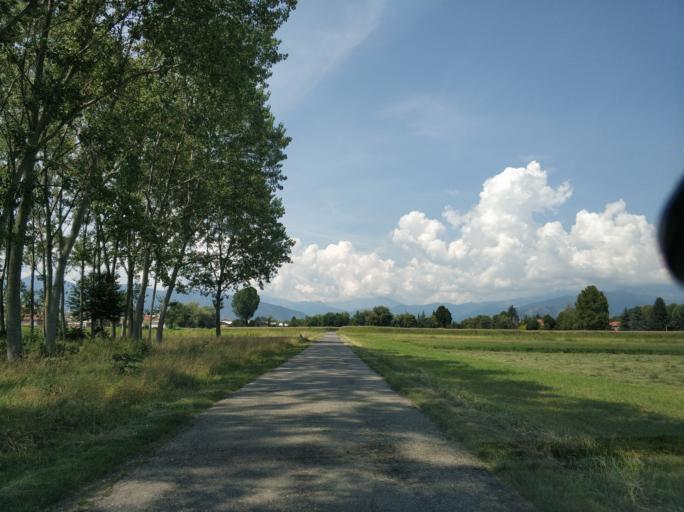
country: IT
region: Piedmont
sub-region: Provincia di Torino
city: San Carlo Canavese
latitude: 45.2369
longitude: 7.6154
